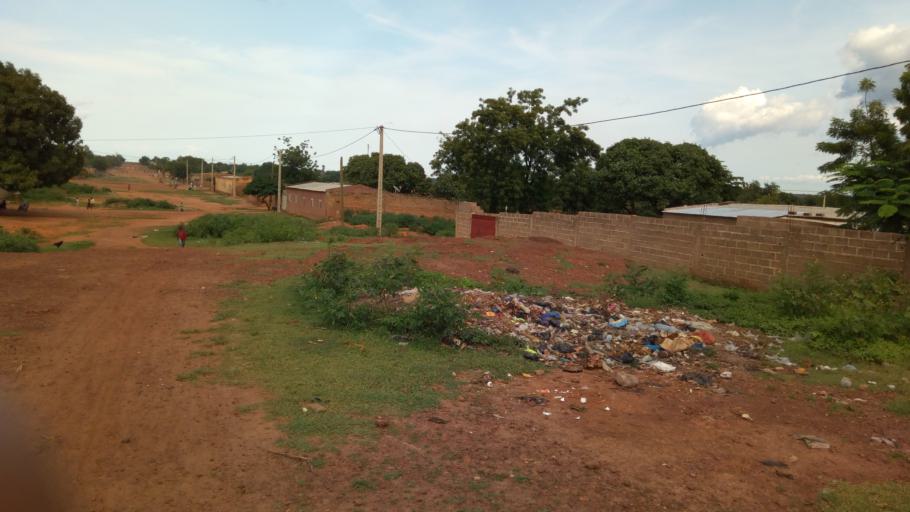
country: ML
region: Sikasso
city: Koutiala
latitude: 12.4105
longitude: -5.4663
